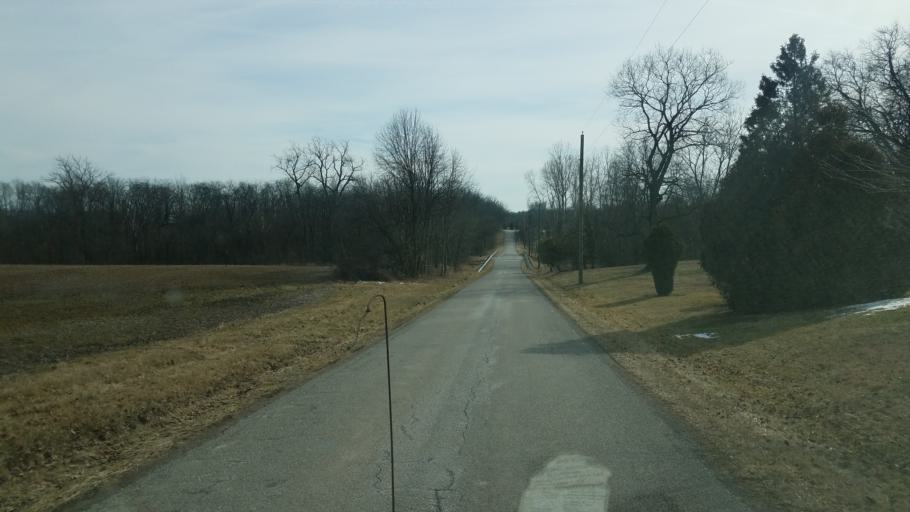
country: US
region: Ohio
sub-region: Union County
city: Marysville
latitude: 40.2957
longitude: -83.3128
